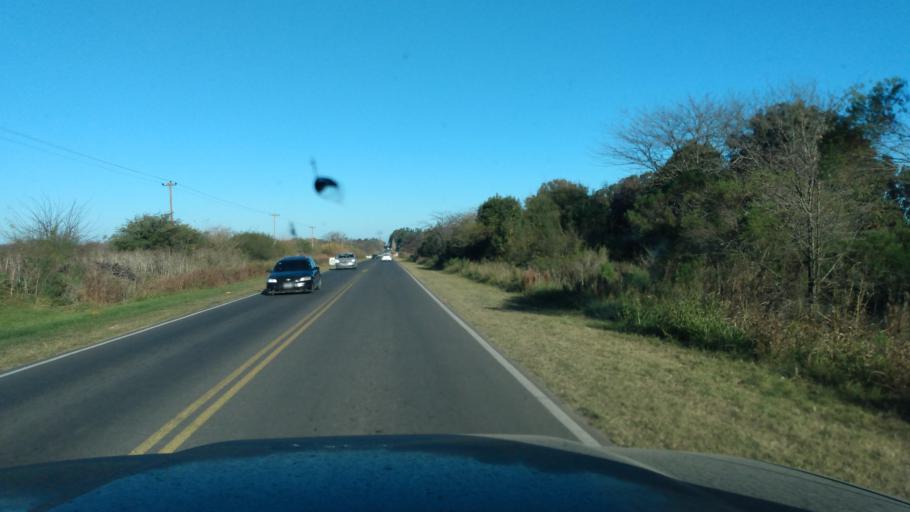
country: AR
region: Buenos Aires
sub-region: Partido de Lujan
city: Lujan
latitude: -34.5205
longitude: -59.1758
